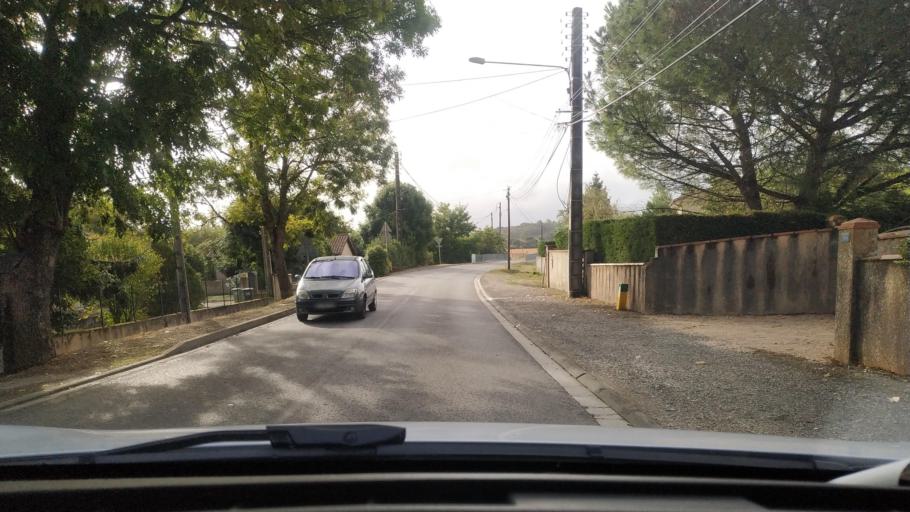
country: FR
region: Midi-Pyrenees
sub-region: Departement de la Haute-Garonne
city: Gaillac-Toulza
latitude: 43.2981
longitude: 1.4707
